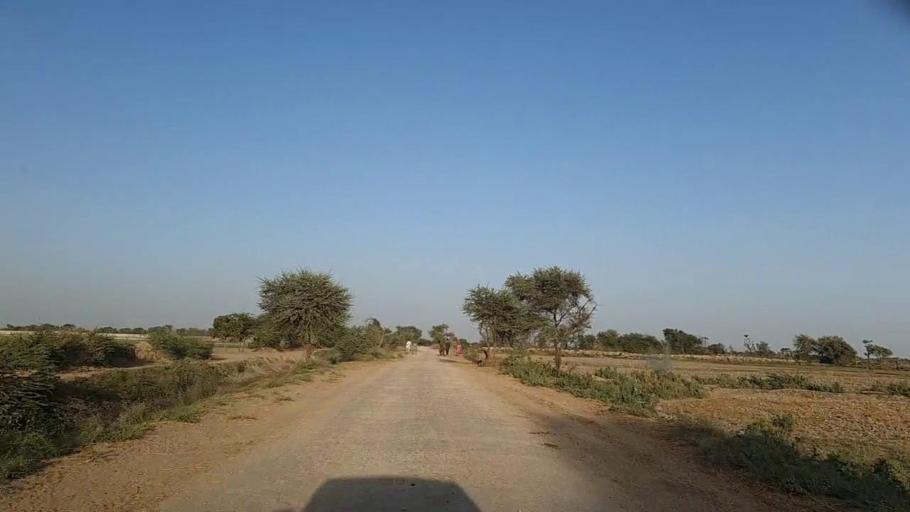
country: PK
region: Sindh
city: Jati
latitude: 24.4147
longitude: 68.3376
